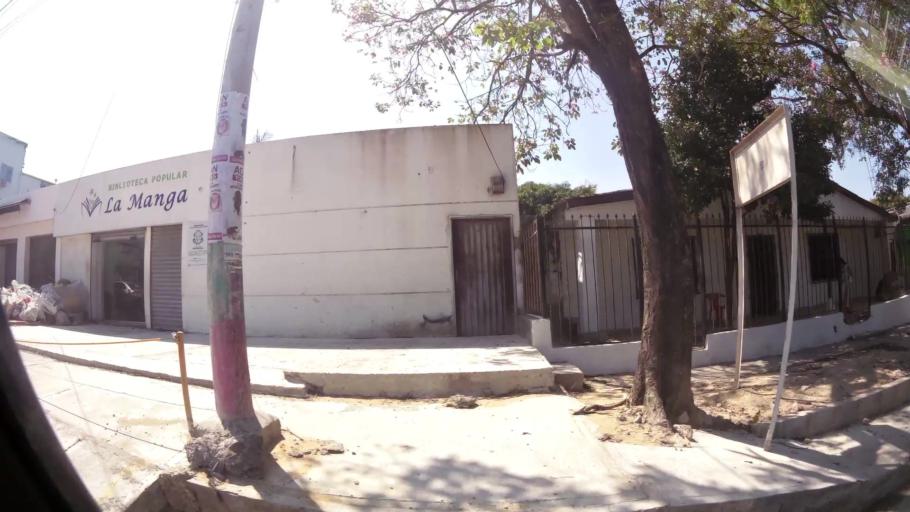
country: CO
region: Atlantico
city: Barranquilla
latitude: 10.9707
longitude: -74.8247
